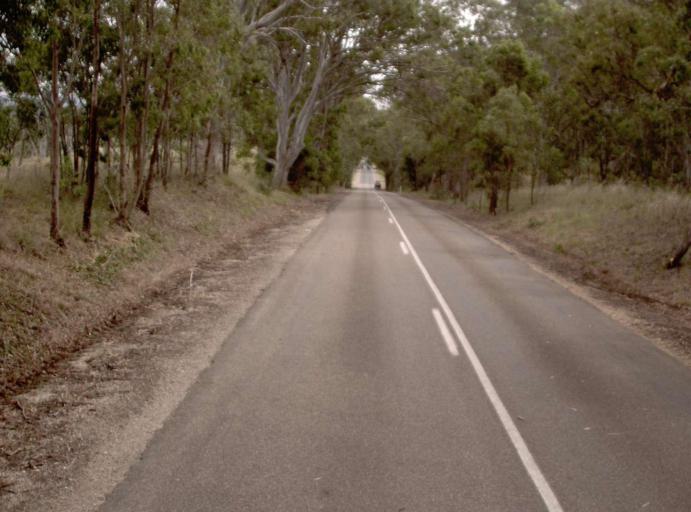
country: AU
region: Victoria
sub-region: Wellington
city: Sale
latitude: -37.8523
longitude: 147.0709
